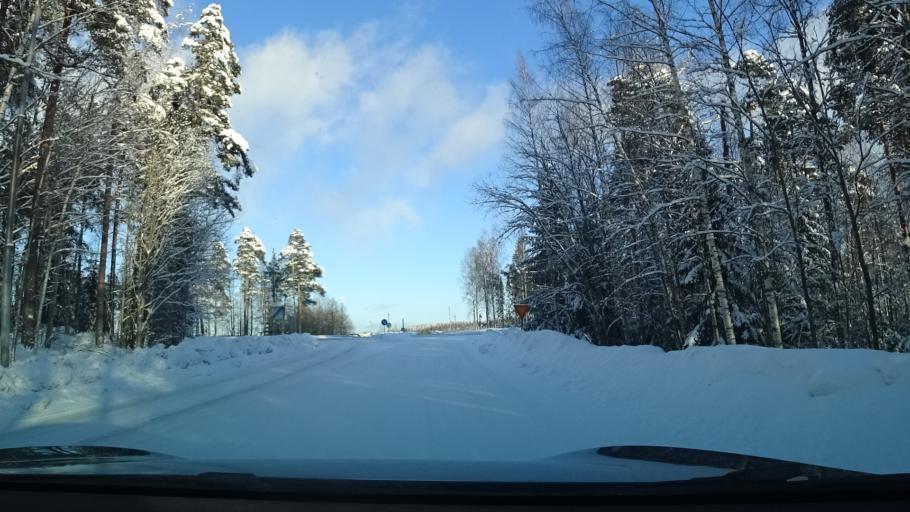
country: FI
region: Northern Savo
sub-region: Varkaus
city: Varkaus
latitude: 62.3097
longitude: 27.9034
